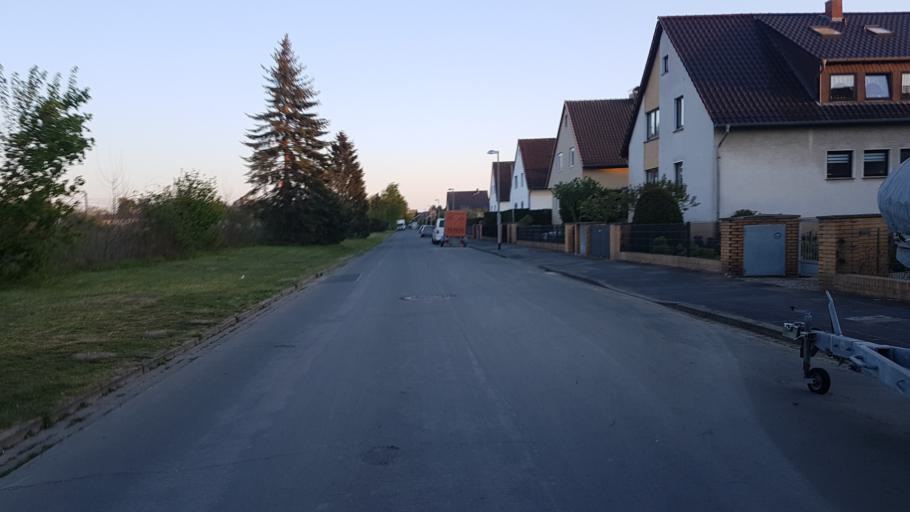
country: DE
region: Lower Saxony
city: Langenhagen
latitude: 52.4238
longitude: 9.7717
